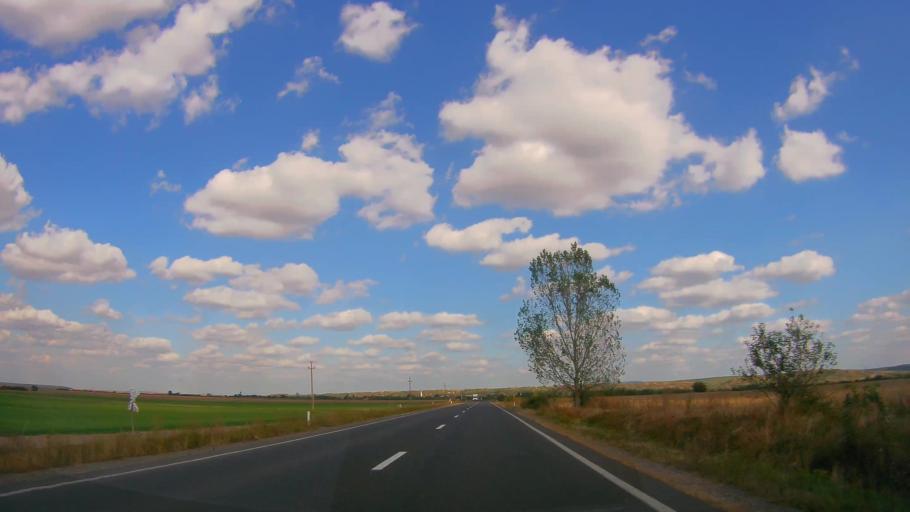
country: RO
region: Satu Mare
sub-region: Comuna Acas
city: Acas
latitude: 47.5400
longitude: 22.8138
